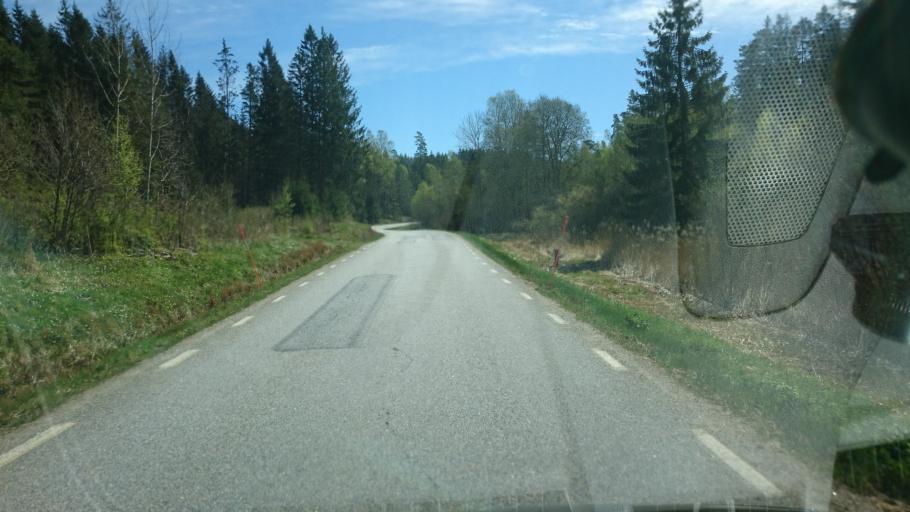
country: SE
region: Vaestra Goetaland
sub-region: Munkedals Kommun
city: Munkedal
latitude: 58.3698
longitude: 11.6916
